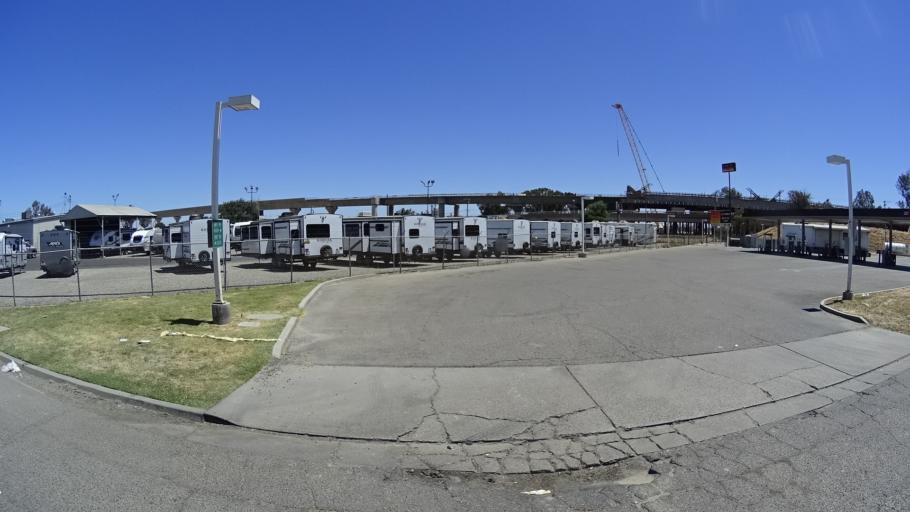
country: US
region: California
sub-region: Fresno County
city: Easton
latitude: 36.6886
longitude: -119.7561
